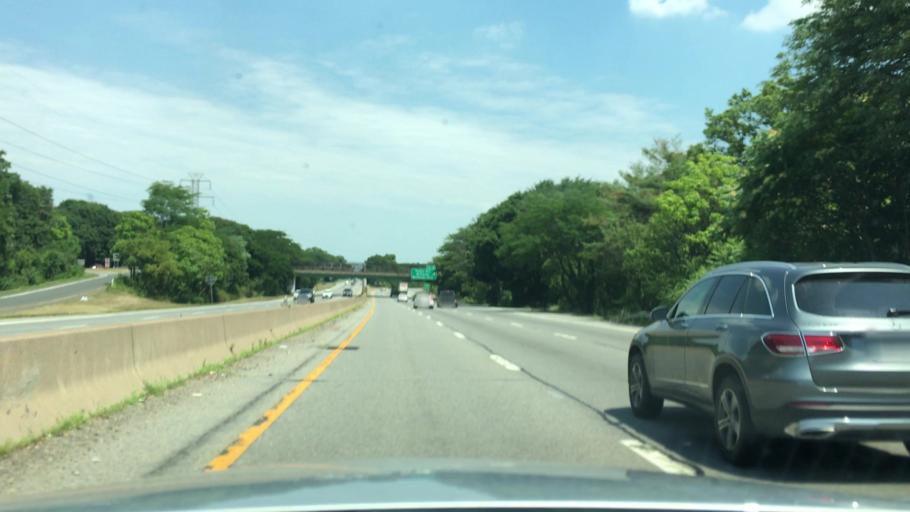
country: US
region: New York
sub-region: Nassau County
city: Bethpage
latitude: 40.7413
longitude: -73.4738
